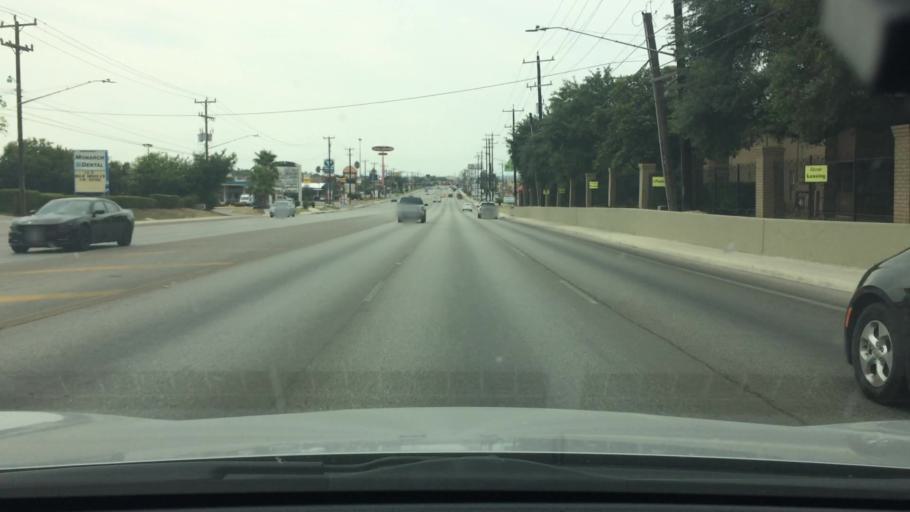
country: US
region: Texas
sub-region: Bexar County
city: Leon Valley
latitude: 29.4623
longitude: -98.6420
